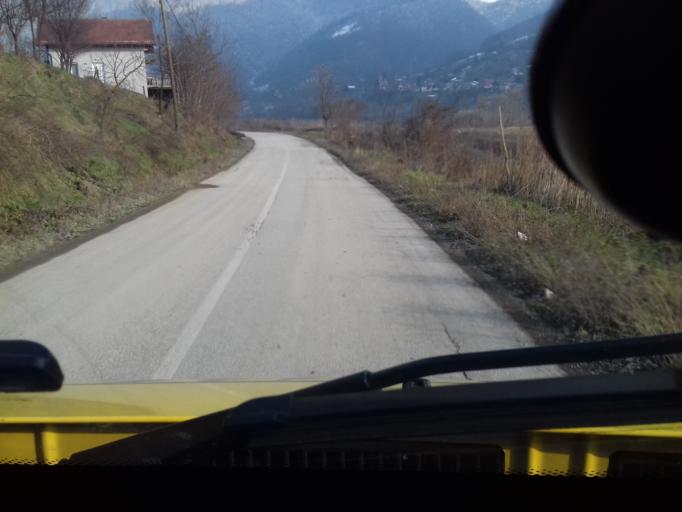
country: BA
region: Federation of Bosnia and Herzegovina
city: Zenica
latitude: 44.2410
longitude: 17.8938
